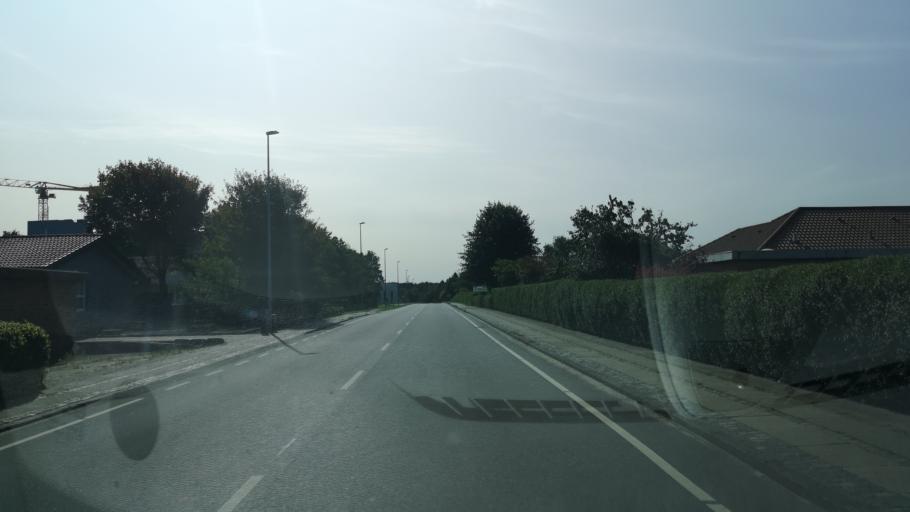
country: DK
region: Central Jutland
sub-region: Ringkobing-Skjern Kommune
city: Videbaek
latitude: 56.0867
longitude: 8.6288
